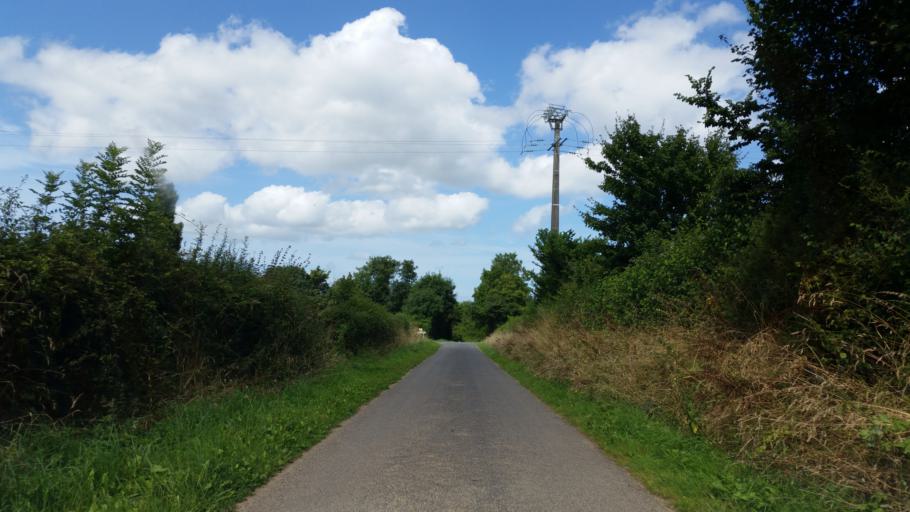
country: FR
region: Lower Normandy
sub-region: Departement de la Manche
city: Montebourg
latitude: 49.4639
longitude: -1.3381
